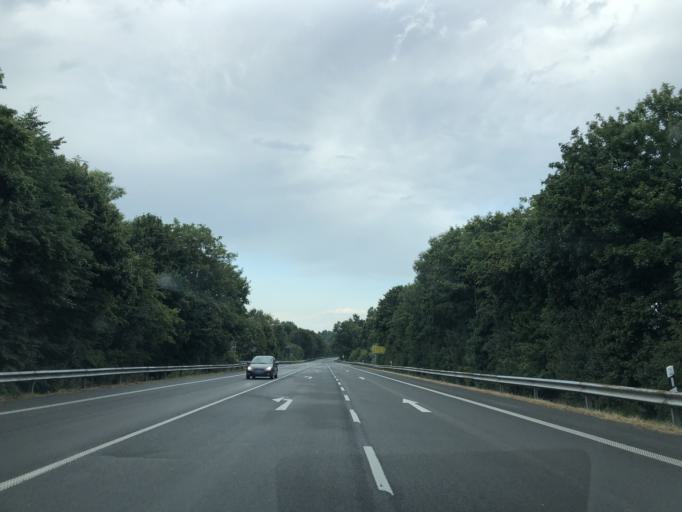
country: DE
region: North Rhine-Westphalia
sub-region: Regierungsbezirk Dusseldorf
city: Kranenburg
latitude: 51.7833
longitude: 6.0276
